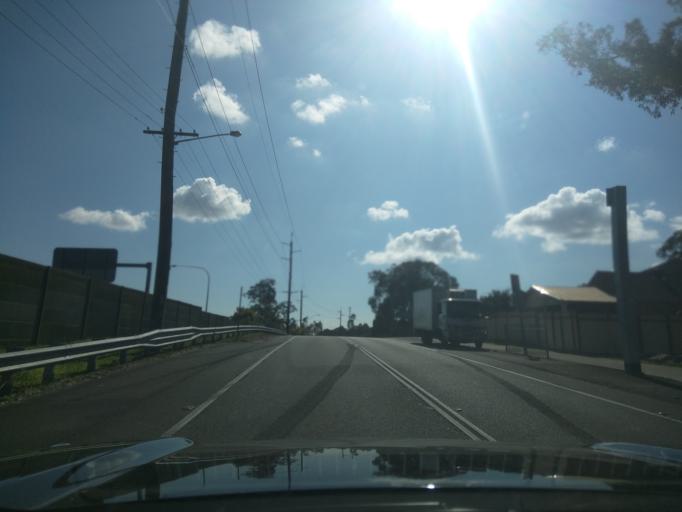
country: AU
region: New South Wales
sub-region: Sutherland Shire
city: Menai
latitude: -34.0222
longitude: 151.0084
